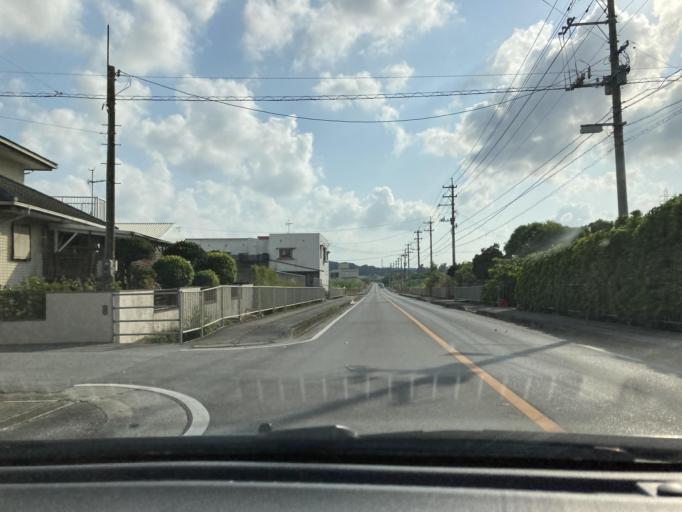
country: JP
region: Okinawa
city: Itoman
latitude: 26.1449
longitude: 127.7041
